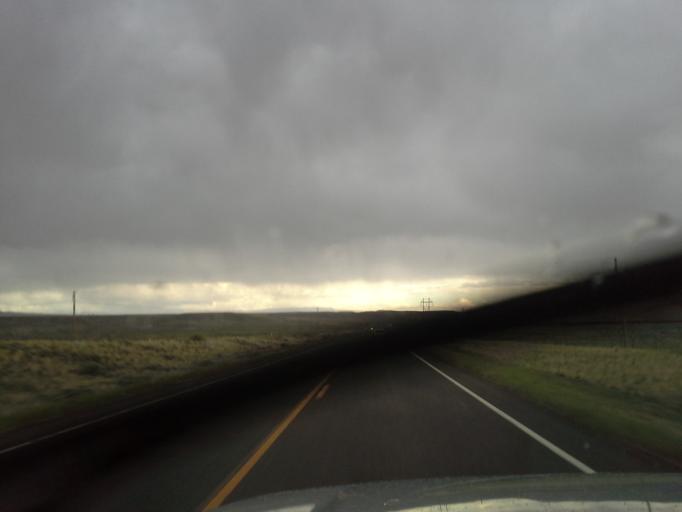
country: US
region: Wyoming
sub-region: Park County
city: Powell
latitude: 45.0679
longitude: -108.6753
